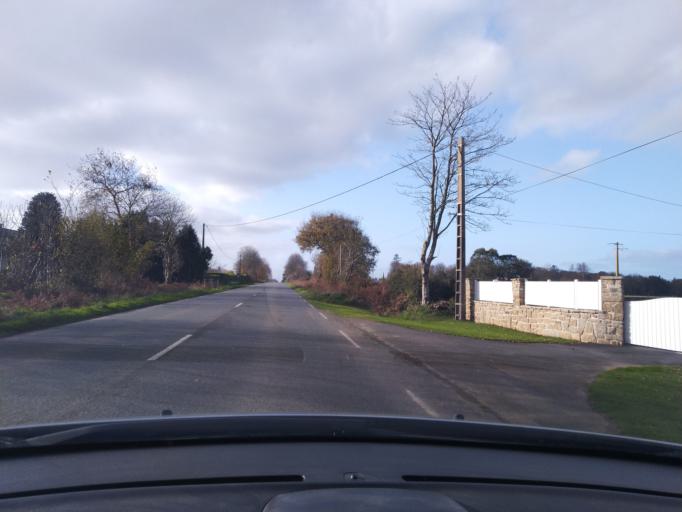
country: FR
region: Brittany
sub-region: Departement du Finistere
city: Plourin-les-Morlaix
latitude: 48.5748
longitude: -3.7569
